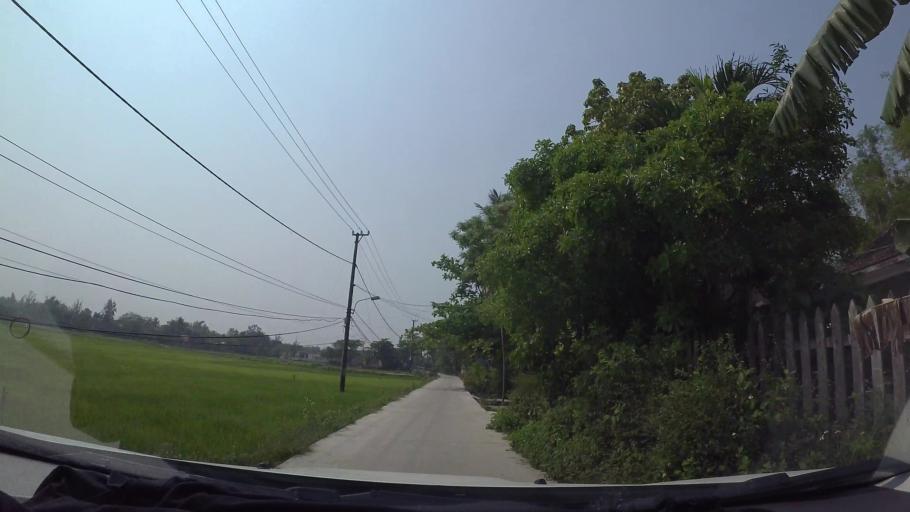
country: VN
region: Da Nang
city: Cam Le
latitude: 15.9803
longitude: 108.2249
